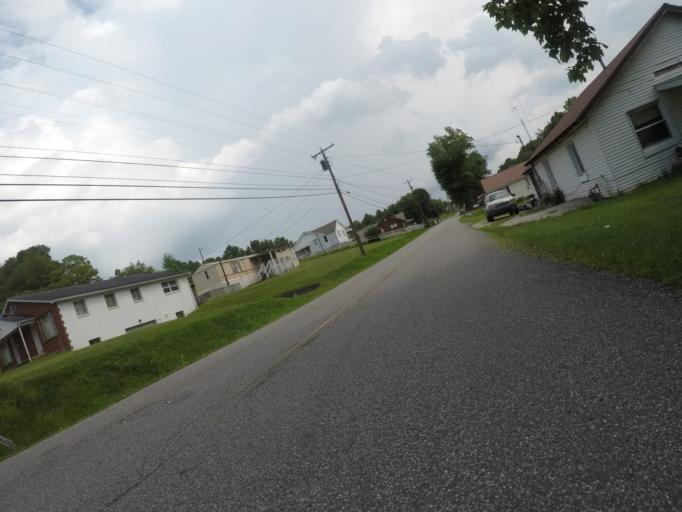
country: US
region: Kentucky
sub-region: Boyd County
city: Meads
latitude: 38.4325
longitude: -82.7088
